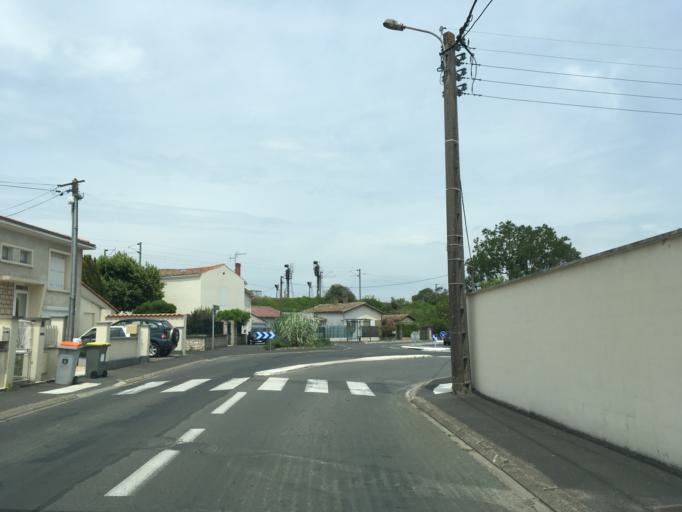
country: FR
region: Poitou-Charentes
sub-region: Departement des Deux-Sevres
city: Niort
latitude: 46.3097
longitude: -0.4612
